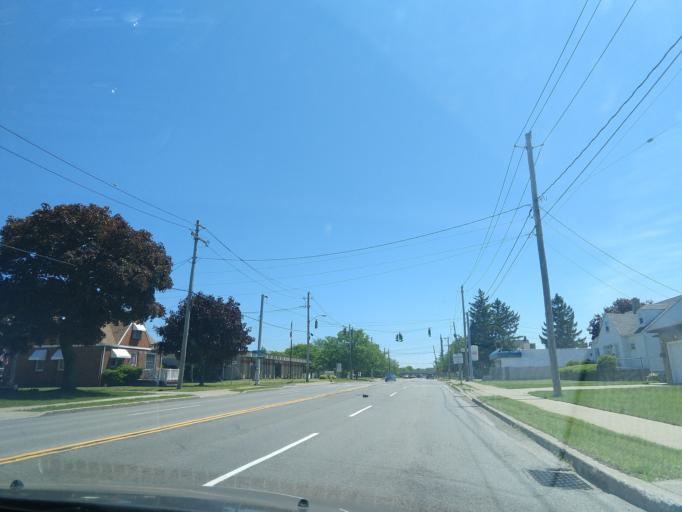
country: US
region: New York
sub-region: Erie County
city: Sloan
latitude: 42.8841
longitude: -78.7731
